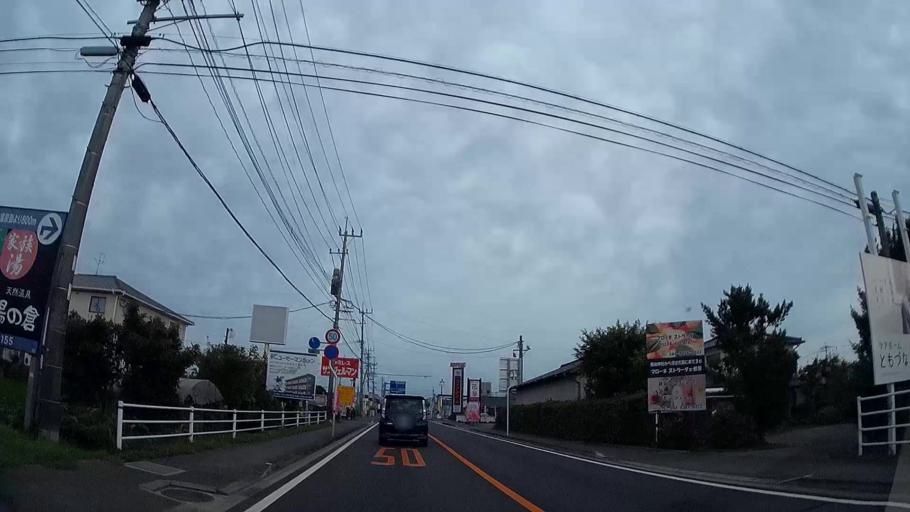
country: JP
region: Kumamoto
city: Kikuchi
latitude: 32.9733
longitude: 130.8091
